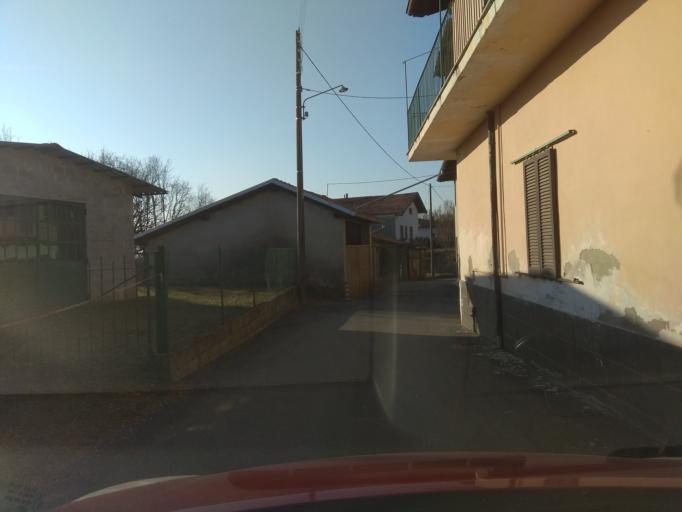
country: IT
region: Piedmont
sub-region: Provincia di Vercelli
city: Roasio
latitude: 45.6015
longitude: 8.2750
